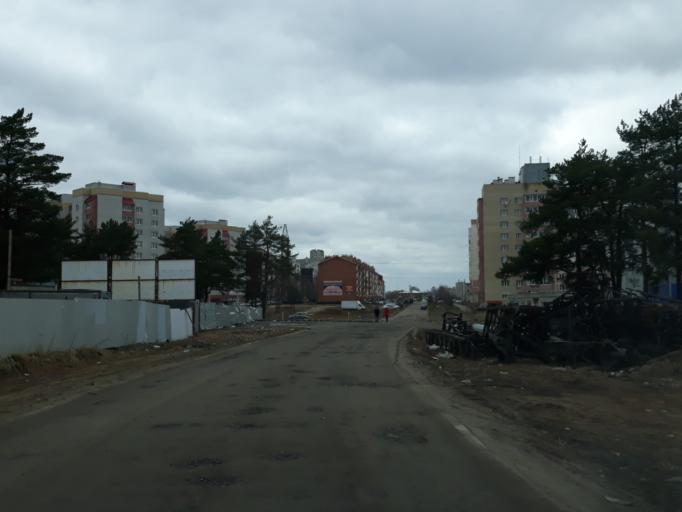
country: RU
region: Jaroslavl
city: Yaroslavl
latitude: 57.6481
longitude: 39.9702
